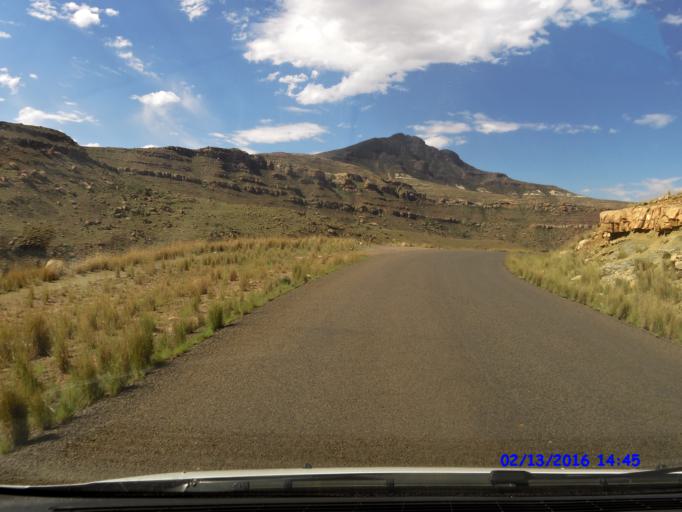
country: LS
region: Qacha's Nek
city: Qacha's Nek
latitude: -30.0647
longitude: 28.3958
